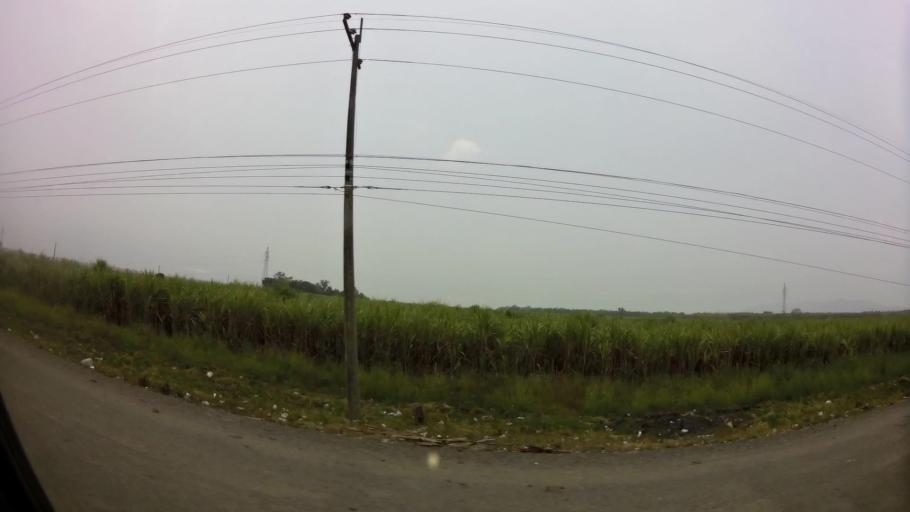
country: HN
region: Cortes
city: La Lima
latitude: 15.4116
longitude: -87.8644
